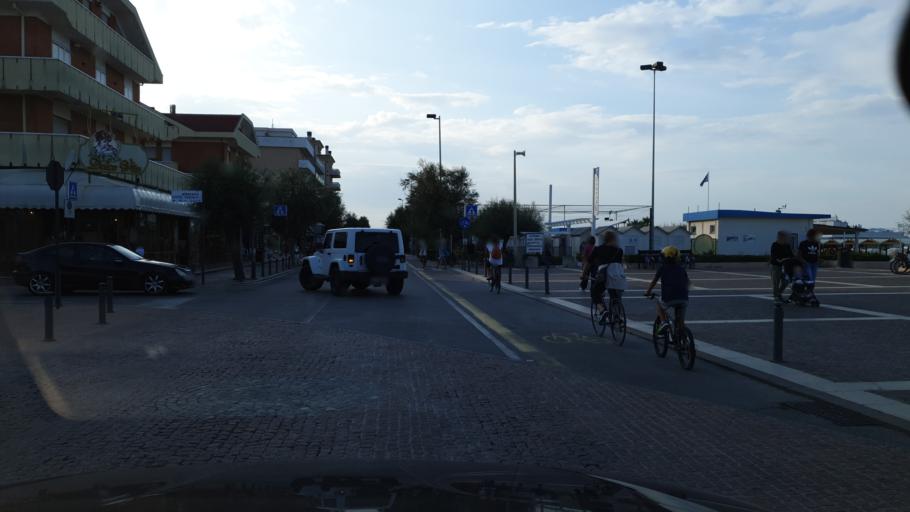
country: IT
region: Emilia-Romagna
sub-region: Provincia di Rimini
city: Misano Adriatico
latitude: 43.9846
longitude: 12.6909
